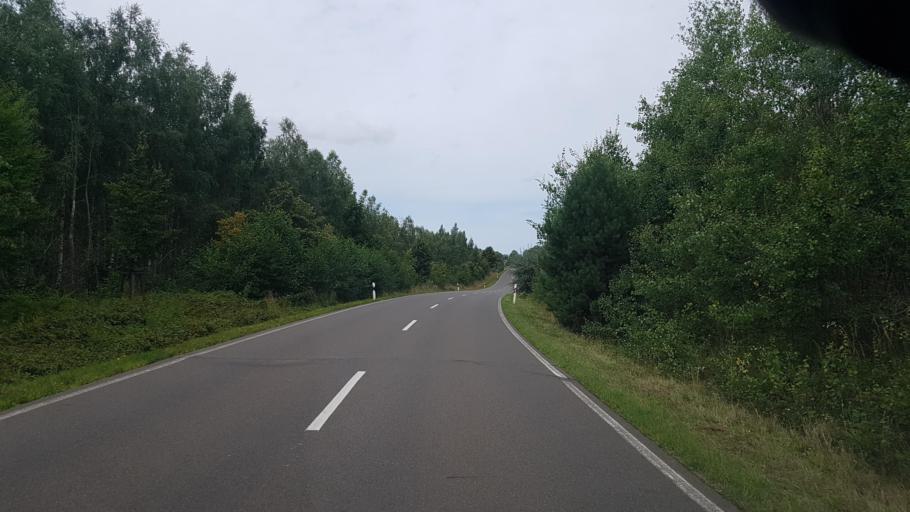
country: DE
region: Brandenburg
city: Spremberg
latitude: 51.5892
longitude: 14.3312
